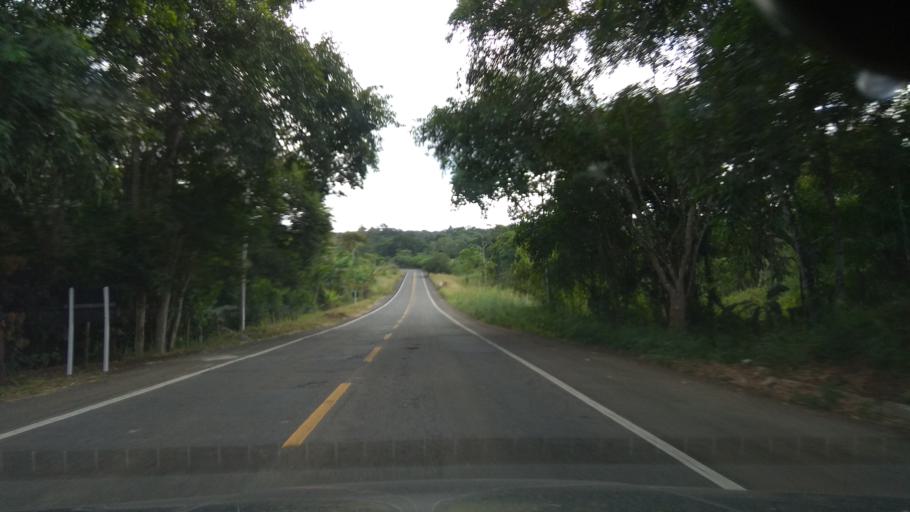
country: BR
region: Bahia
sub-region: Ubaitaba
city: Ubaitaba
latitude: -14.2643
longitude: -39.3305
